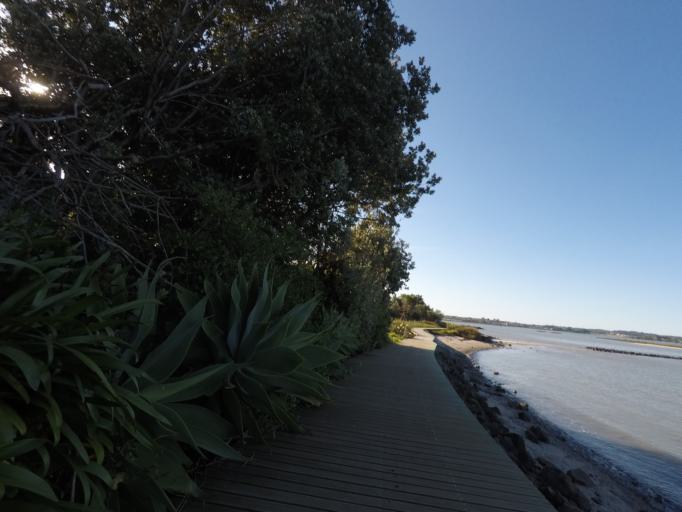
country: NZ
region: Auckland
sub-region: Auckland
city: Rosebank
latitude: -36.8317
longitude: 174.6607
